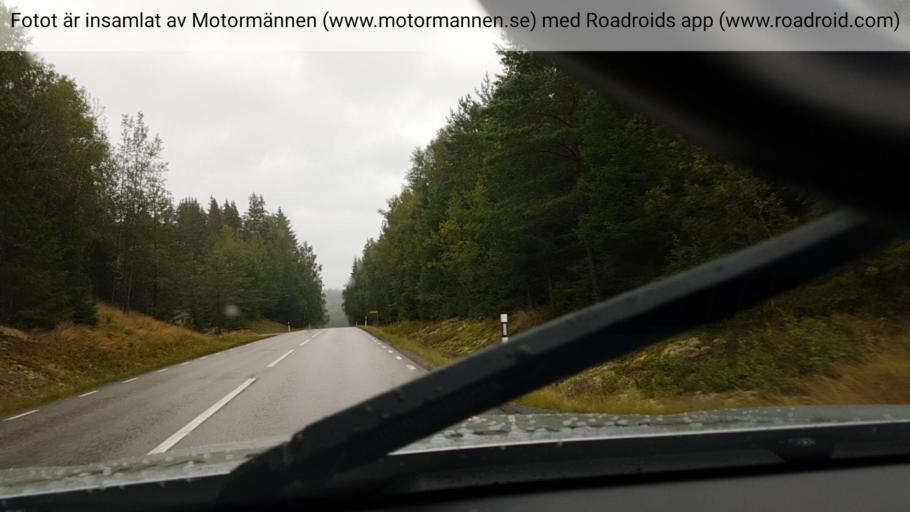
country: SE
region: Vaestra Goetaland
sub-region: Bengtsfors Kommun
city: Dals Langed
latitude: 58.9089
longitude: 12.2205
